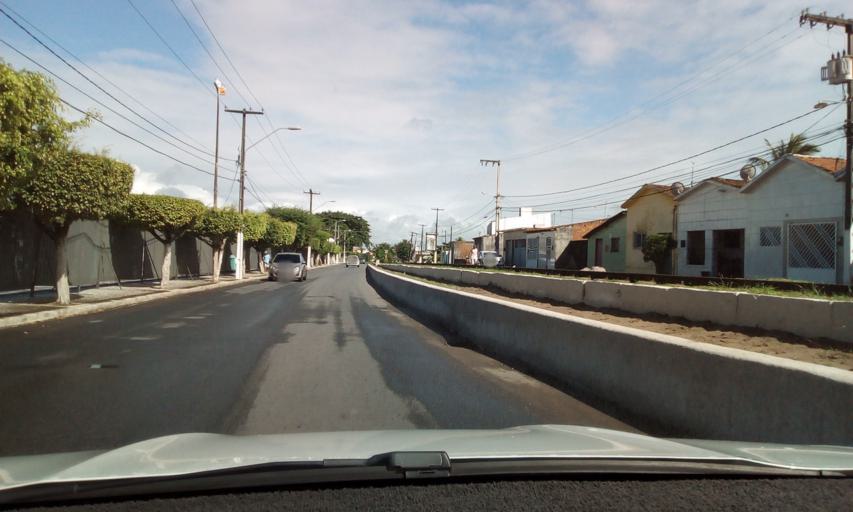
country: BR
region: Paraiba
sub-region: Santa Rita
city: Santa Rita
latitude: -7.1238
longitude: -34.9722
